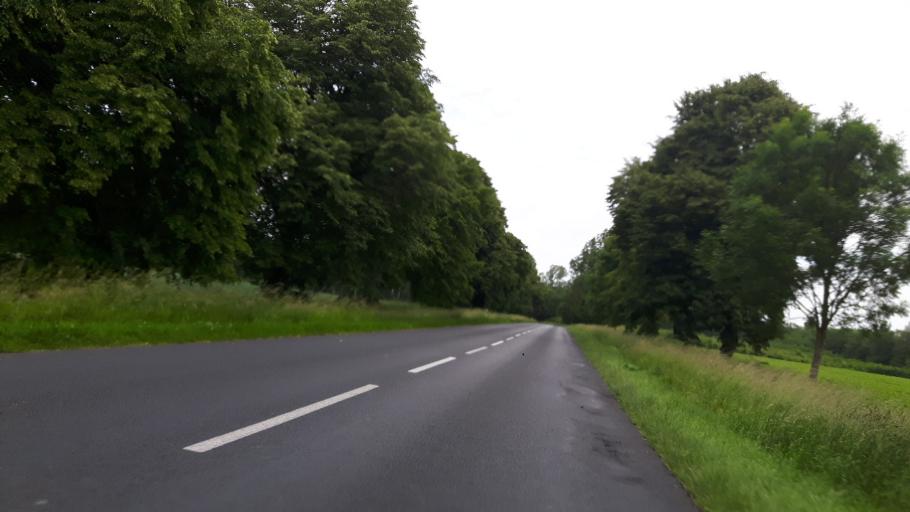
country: PL
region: West Pomeranian Voivodeship
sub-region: Powiat gryficki
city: Trzebiatow
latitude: 53.9858
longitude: 15.2402
